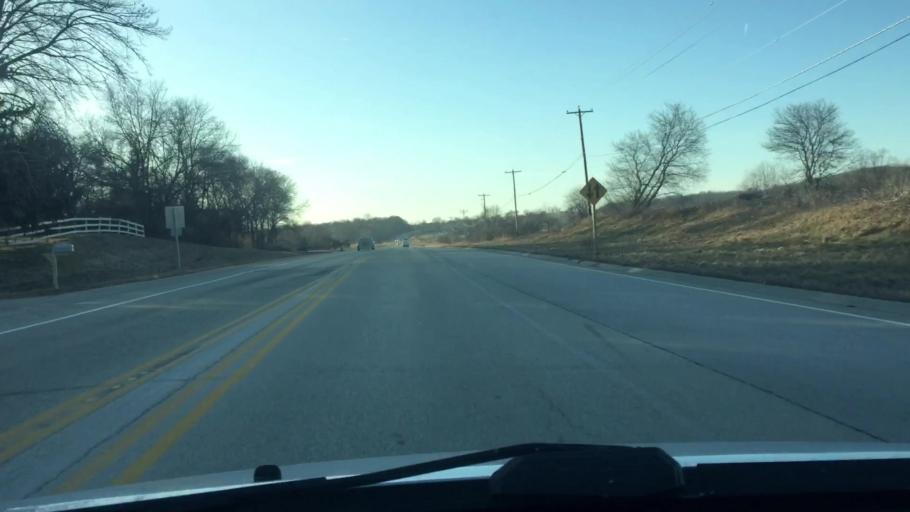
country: US
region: Wisconsin
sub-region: Waukesha County
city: Pewaukee
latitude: 43.1123
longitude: -88.2488
